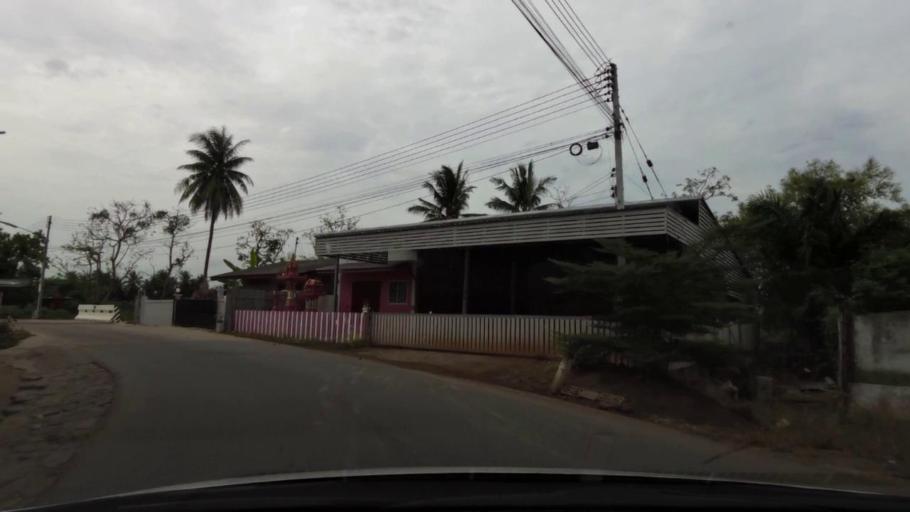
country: TH
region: Ratchaburi
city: Damnoen Saduak
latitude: 13.5748
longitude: 99.9925
